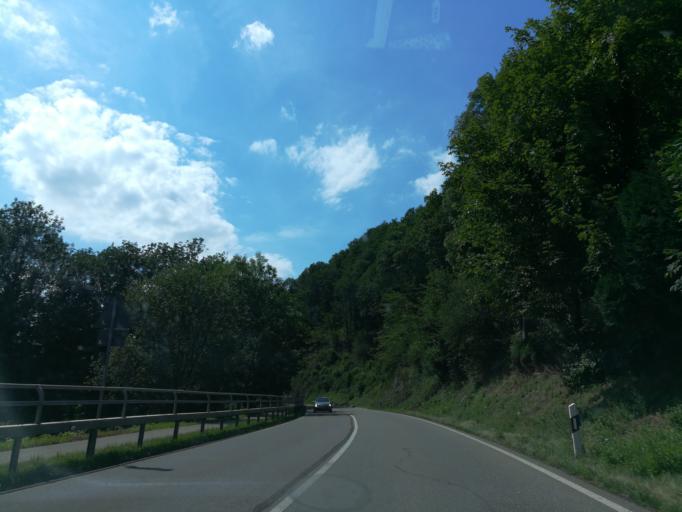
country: DE
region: Baden-Wuerttemberg
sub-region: Freiburg Region
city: Wolfach
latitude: 48.2847
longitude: 8.2019
